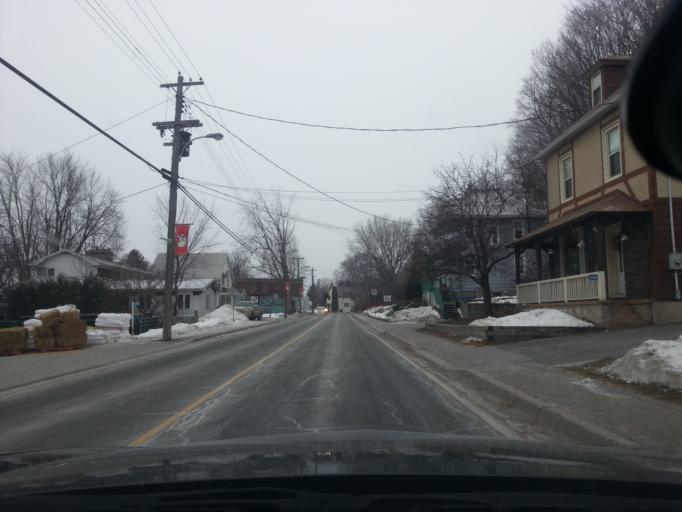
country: CA
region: Ontario
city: Arnprior
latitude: 45.3352
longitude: -76.2889
